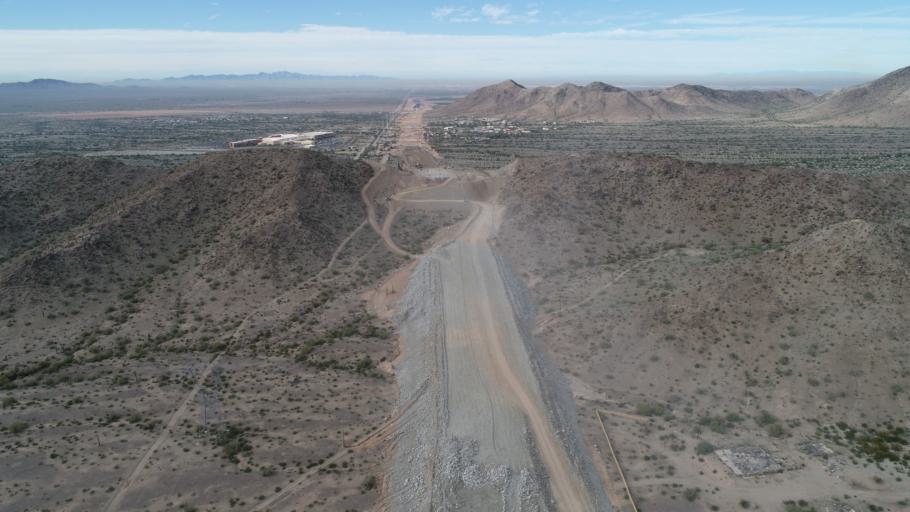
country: US
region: Arizona
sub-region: Maricopa County
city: Laveen
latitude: 33.2999
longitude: -112.1412
